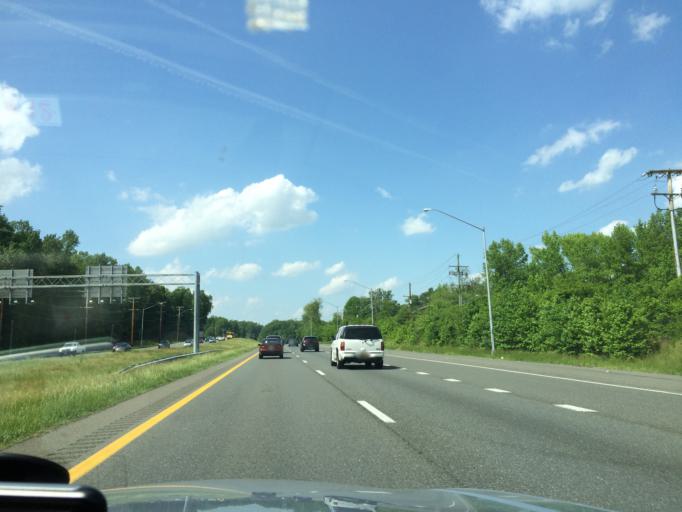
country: US
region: Maryland
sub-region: Prince George's County
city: Bowie
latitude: 38.9667
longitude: -76.7165
